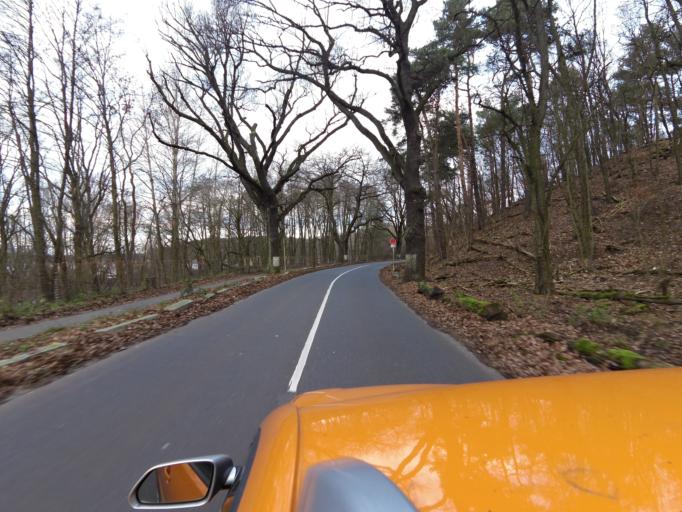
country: DE
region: Berlin
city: Gatow
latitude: 52.4678
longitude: 13.1966
